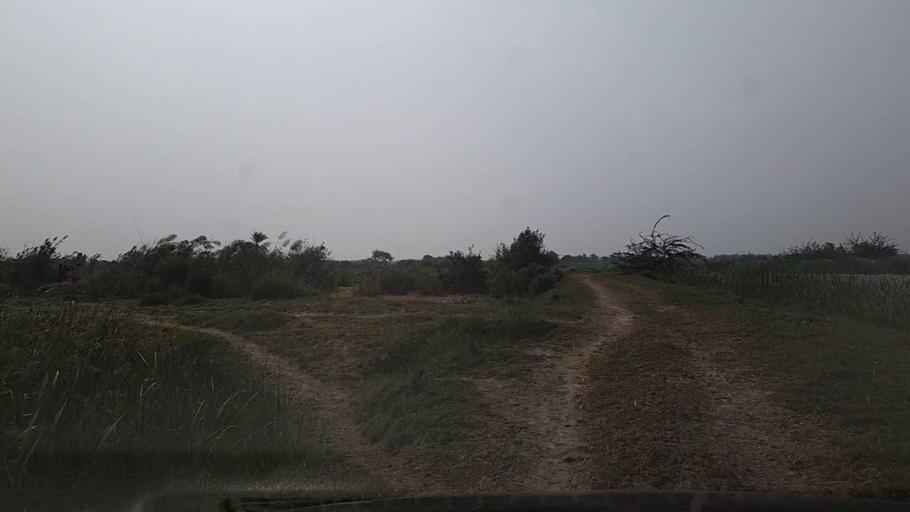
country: PK
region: Sindh
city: Thatta
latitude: 24.7607
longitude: 67.8049
